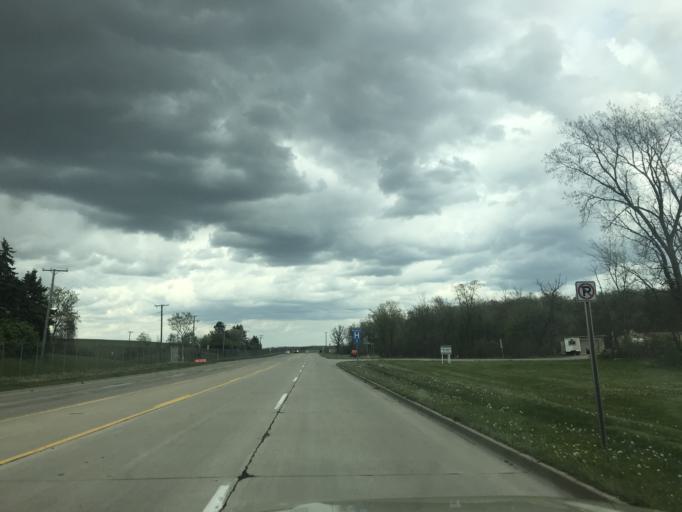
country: US
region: Michigan
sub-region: Wayne County
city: Romulus
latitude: 42.1932
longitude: -83.3466
